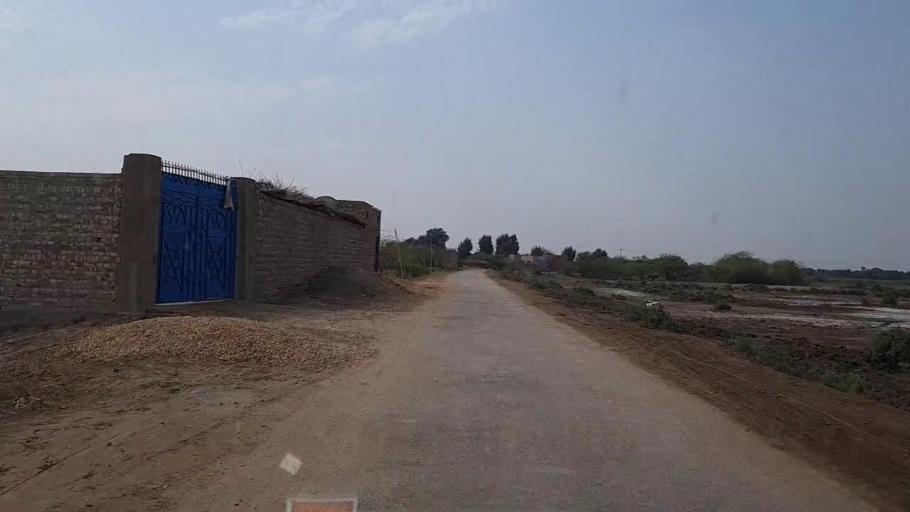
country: PK
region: Sindh
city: Mirwah Gorchani
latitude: 25.3283
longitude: 69.0367
